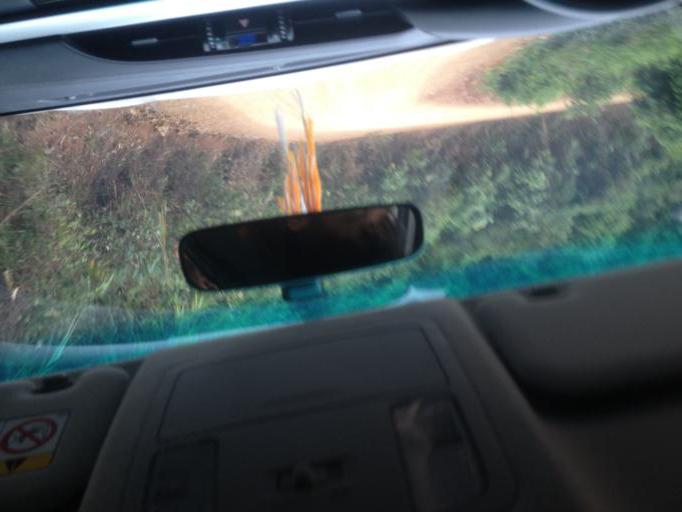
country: TH
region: Nan
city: Chaloem Phra Kiat
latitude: 19.9902
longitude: 101.1408
